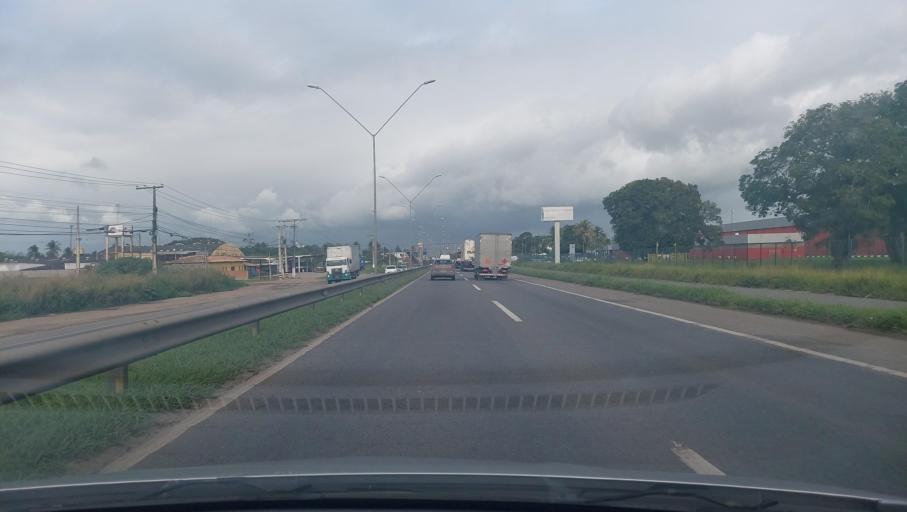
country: BR
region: Bahia
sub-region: Feira De Santana
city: Feira de Santana
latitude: -12.3118
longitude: -38.8833
